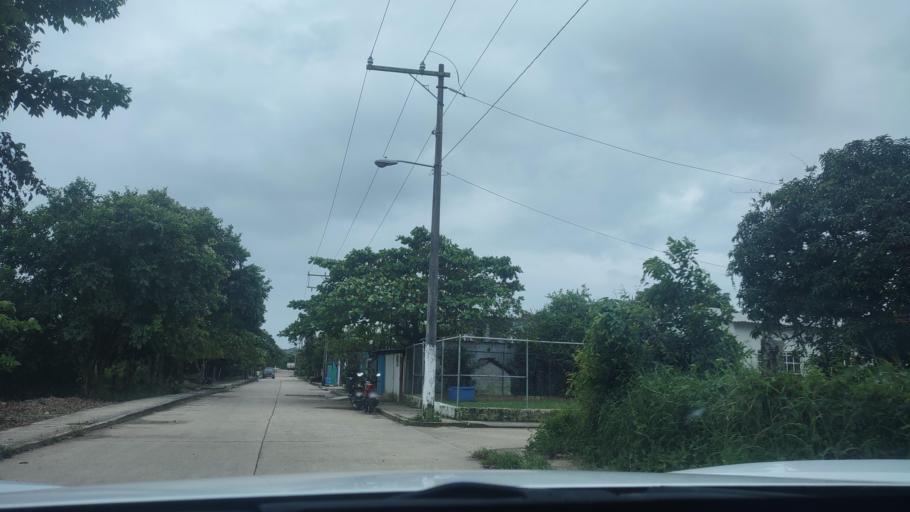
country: MX
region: Veracruz
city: Villa Nanchital
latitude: 18.0426
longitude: -94.3496
